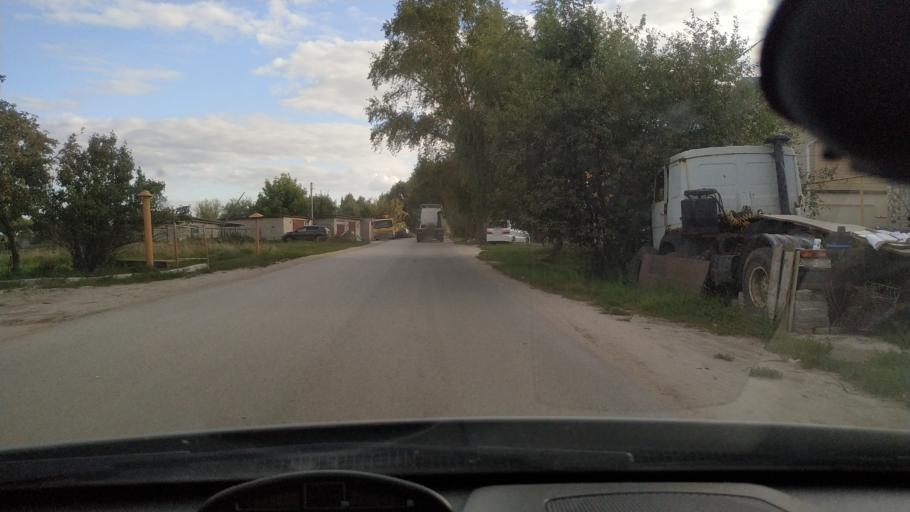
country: RU
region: Rjazan
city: Polyany
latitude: 54.5827
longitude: 39.8394
